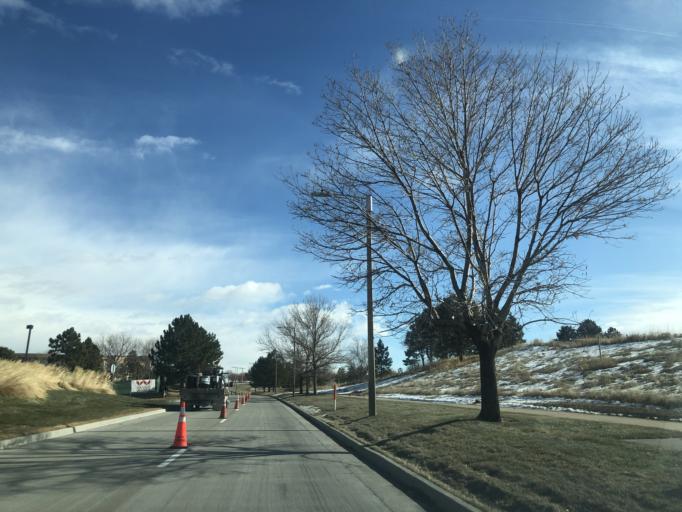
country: US
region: Colorado
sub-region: Douglas County
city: Meridian
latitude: 39.5481
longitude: -104.8482
